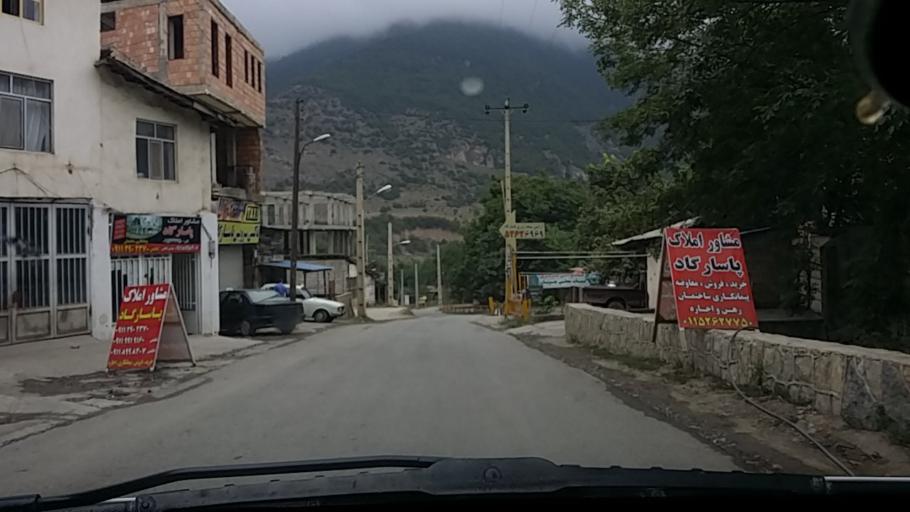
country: IR
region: Mazandaran
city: `Abbasabad
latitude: 36.4841
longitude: 51.1354
